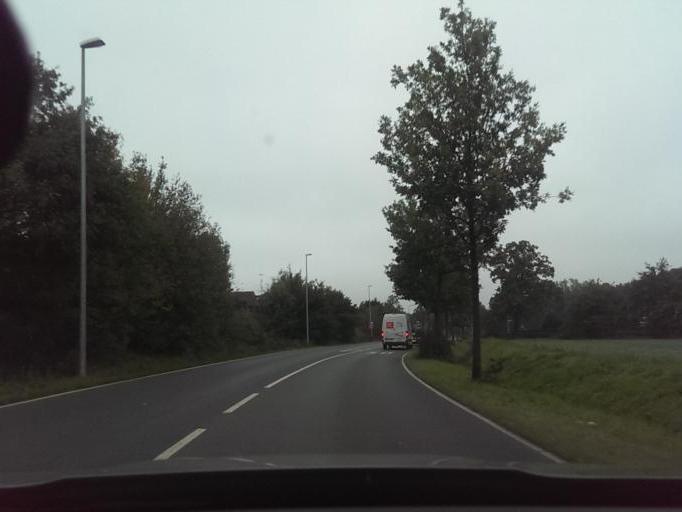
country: DE
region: Lower Saxony
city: Garbsen-Mitte
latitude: 52.4346
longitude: 9.6203
